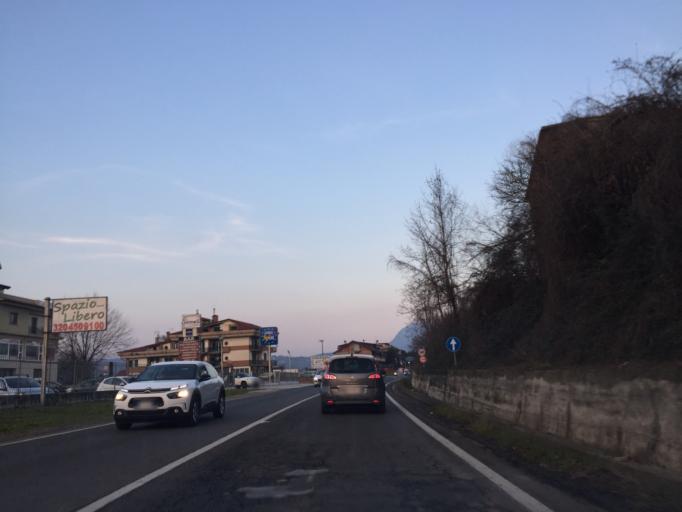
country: IT
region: Campania
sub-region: Provincia di Avellino
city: Atripalda
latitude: 40.9113
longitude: 14.8147
